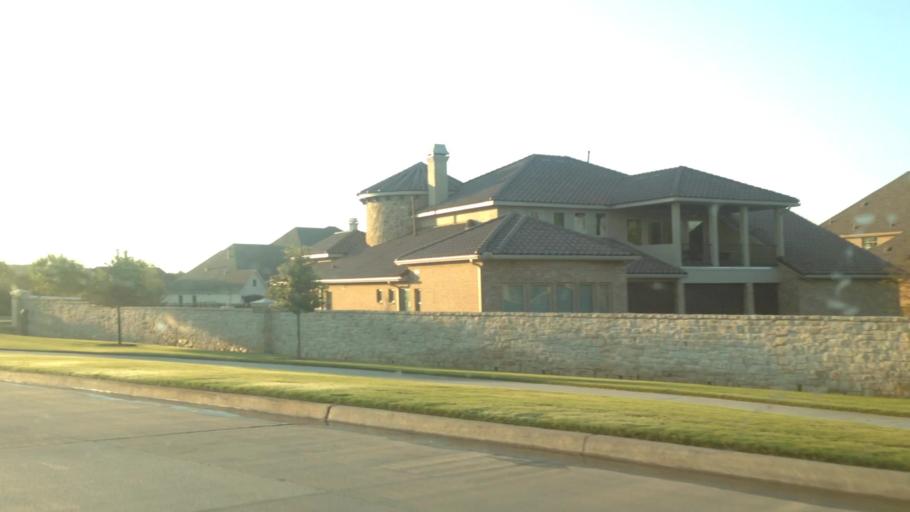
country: US
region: Texas
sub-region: Tarrant County
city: Southlake
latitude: 32.9385
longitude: -97.1365
